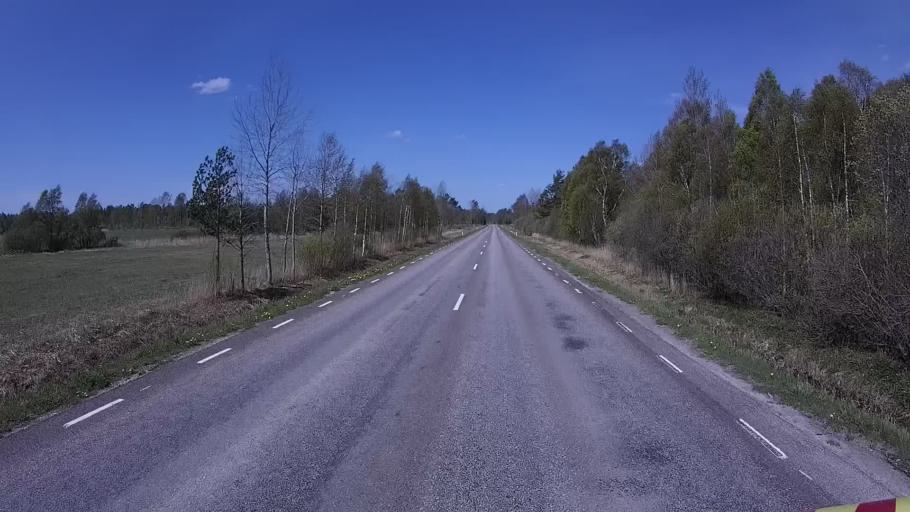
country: EE
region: Laeaene
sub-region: Ridala Parish
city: Uuemoisa
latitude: 58.8978
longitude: 23.5859
